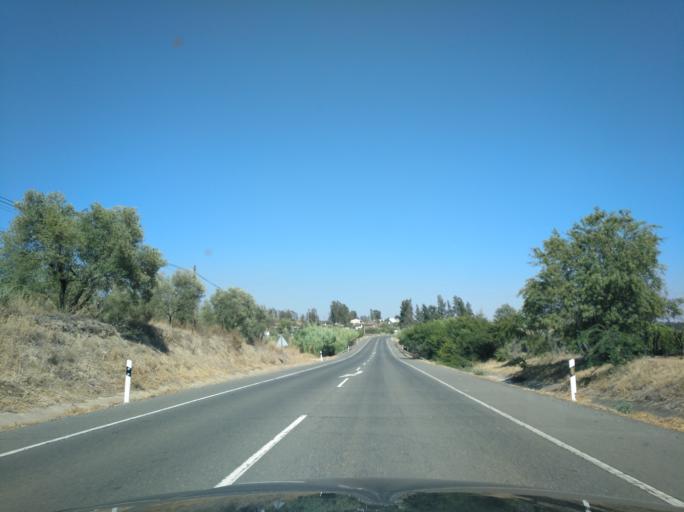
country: ES
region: Andalusia
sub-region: Provincia de Huelva
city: Gibraleon
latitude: 37.3552
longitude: -7.0057
